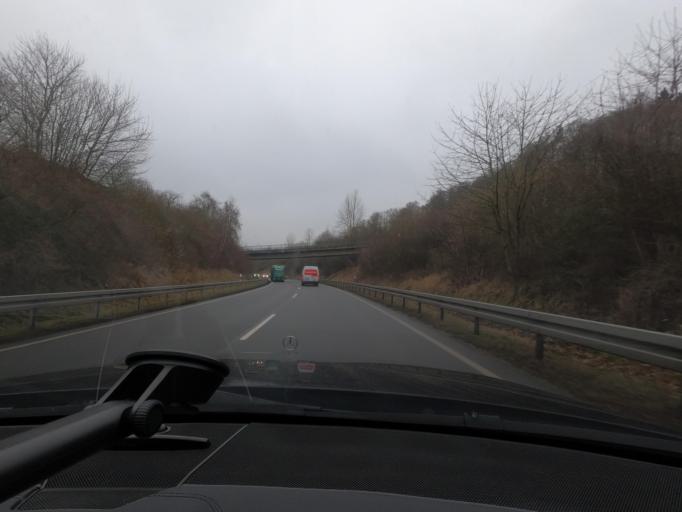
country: DE
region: Hesse
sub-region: Regierungsbezirk Kassel
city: Bad Arolsen
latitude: 51.3853
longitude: 8.9938
